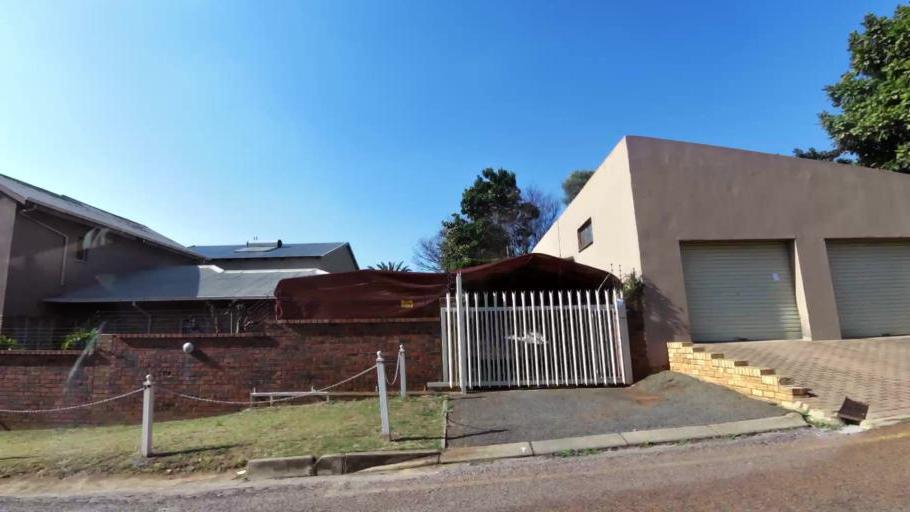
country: ZA
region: Gauteng
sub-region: City of Johannesburg Metropolitan Municipality
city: Johannesburg
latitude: -26.1782
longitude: 27.9936
